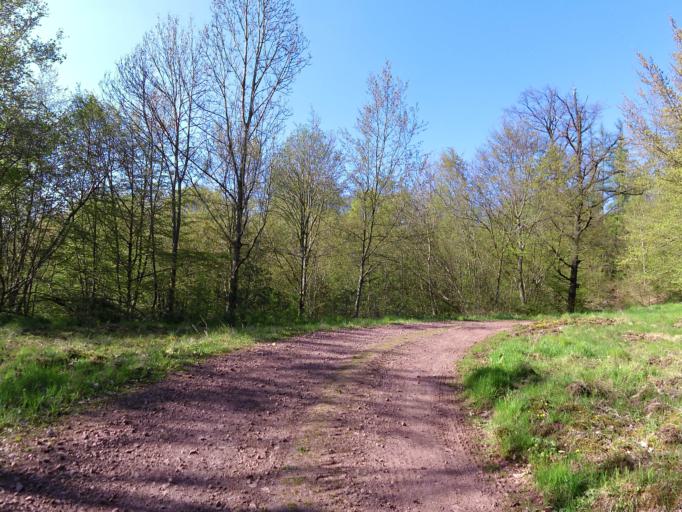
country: DE
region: Thuringia
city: Wolfsburg-Unkeroda
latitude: 50.9370
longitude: 10.2717
